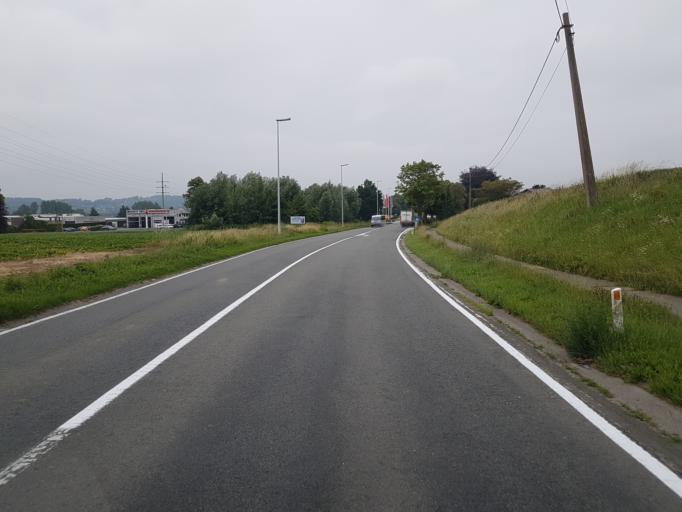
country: BE
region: Flanders
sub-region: Provincie Oost-Vlaanderen
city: Geraardsbergen
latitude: 50.7953
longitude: 3.8731
